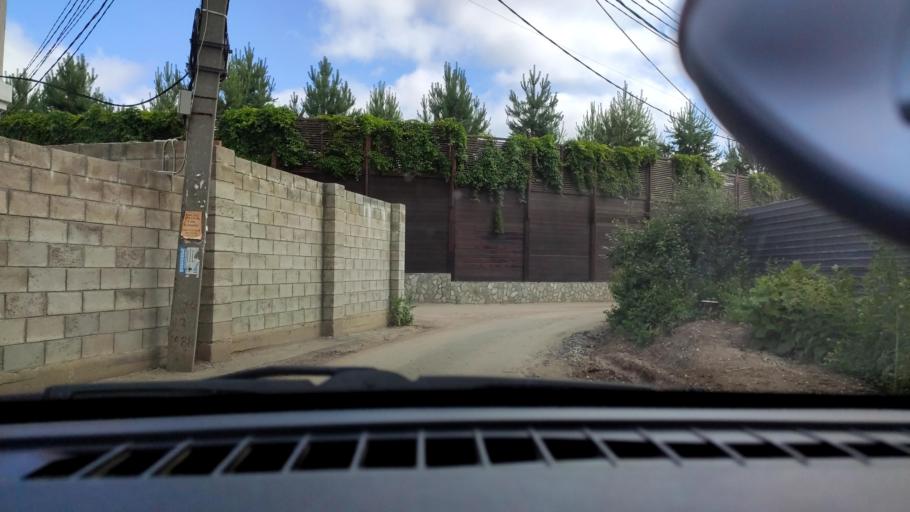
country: RU
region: Samara
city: Novokuybyshevsk
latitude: 53.1514
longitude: 49.9670
